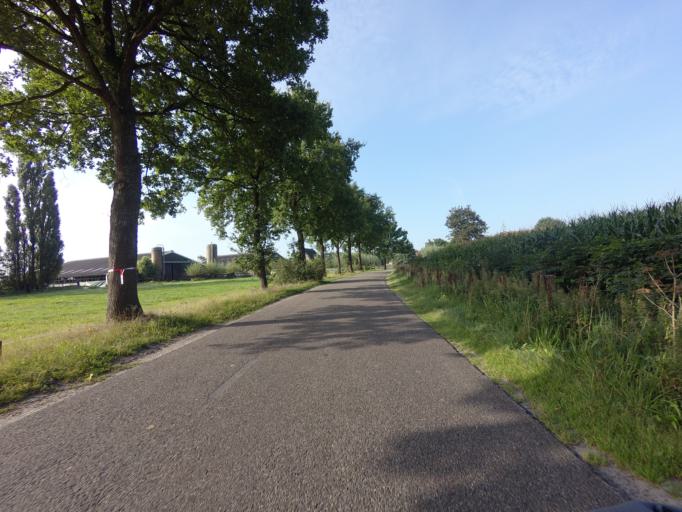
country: NL
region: Friesland
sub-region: Gemeente Weststellingwerf
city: Noordwolde
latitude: 52.9144
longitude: 6.1575
